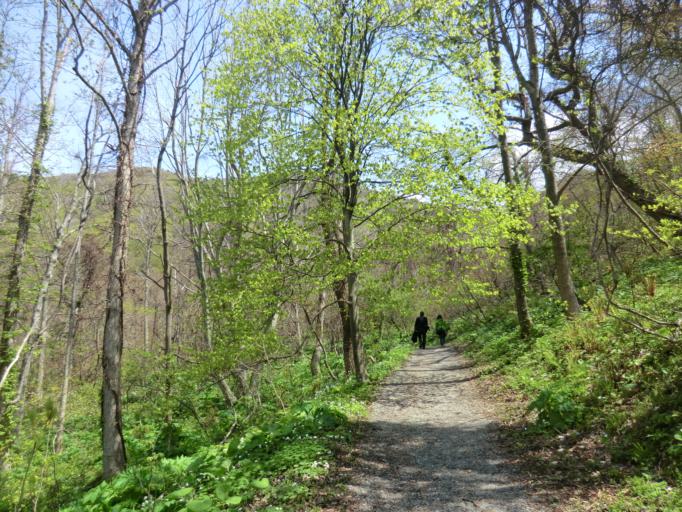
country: JP
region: Aomori
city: Mutsu
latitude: 41.3110
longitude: 140.8082
